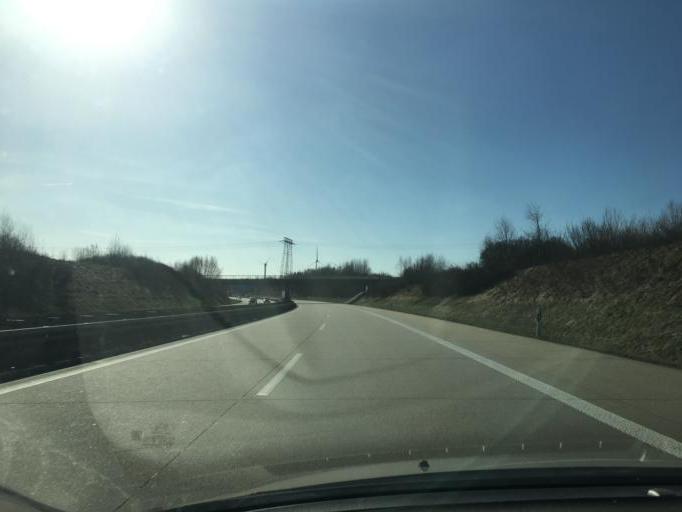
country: DE
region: Saxony
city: Hartmannsdorf
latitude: 50.8590
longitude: 12.8195
